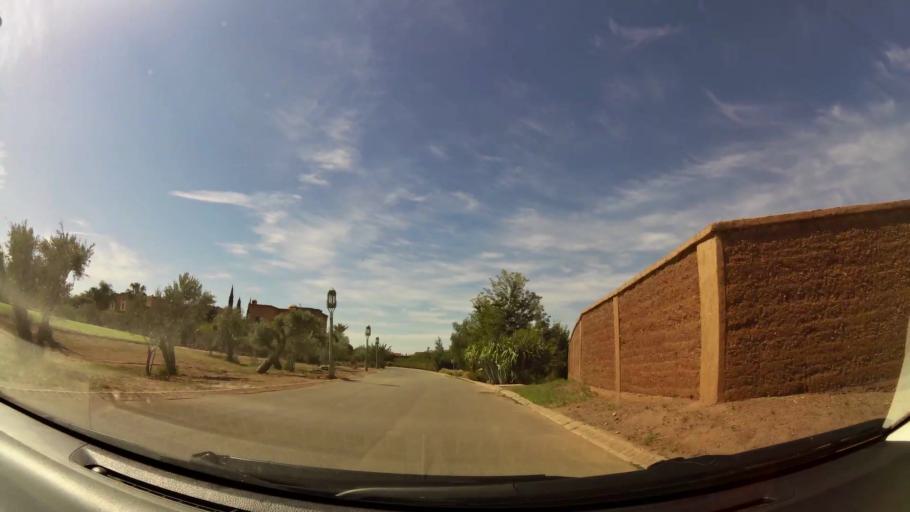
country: MA
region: Marrakech-Tensift-Al Haouz
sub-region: Marrakech
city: Marrakesh
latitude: 31.6198
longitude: -7.9385
